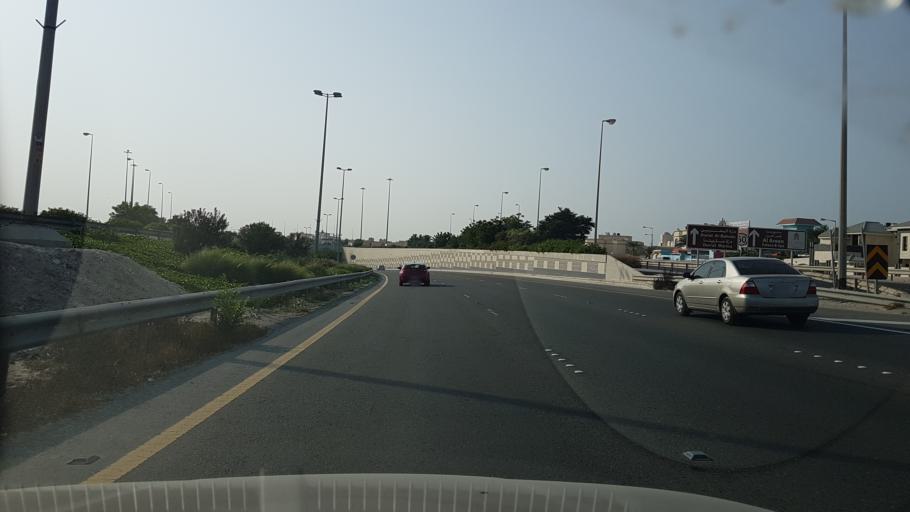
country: BH
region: Central Governorate
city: Madinat Hamad
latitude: 26.1244
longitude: 50.5061
